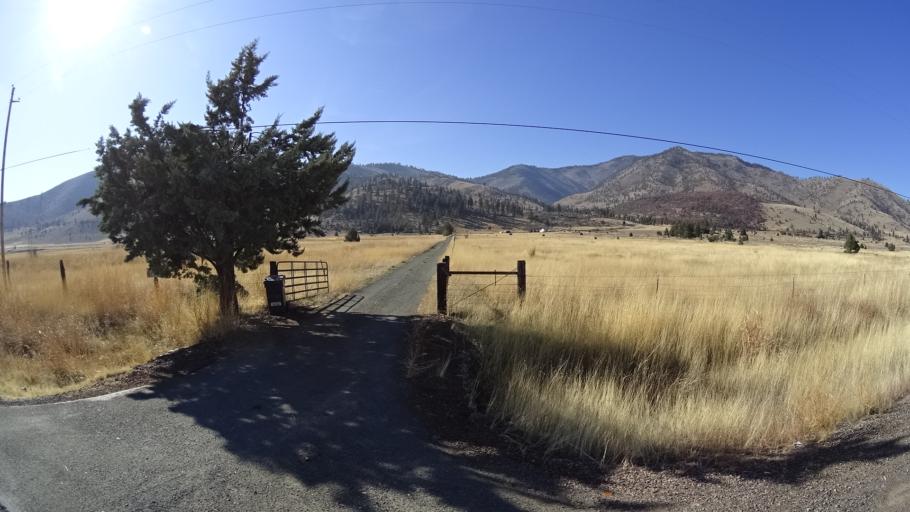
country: US
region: California
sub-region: Siskiyou County
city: Weed
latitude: 41.4748
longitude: -122.4834
